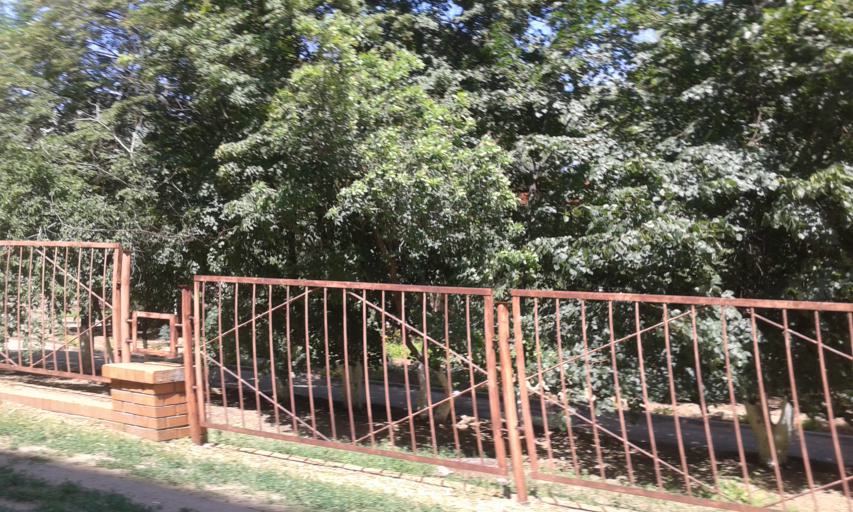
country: RU
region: Volgograd
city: Volgograd
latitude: 48.7524
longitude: 44.5085
